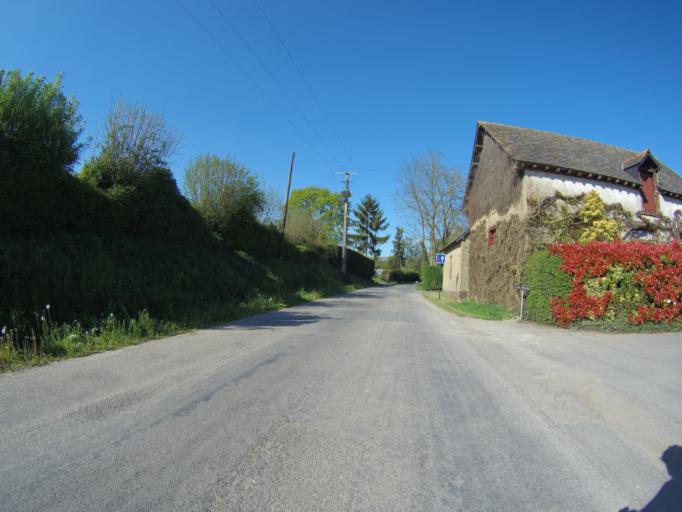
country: FR
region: Brittany
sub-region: Departement d'Ille-et-Vilaine
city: Vern-sur-Seiche
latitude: 48.0488
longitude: -1.6191
